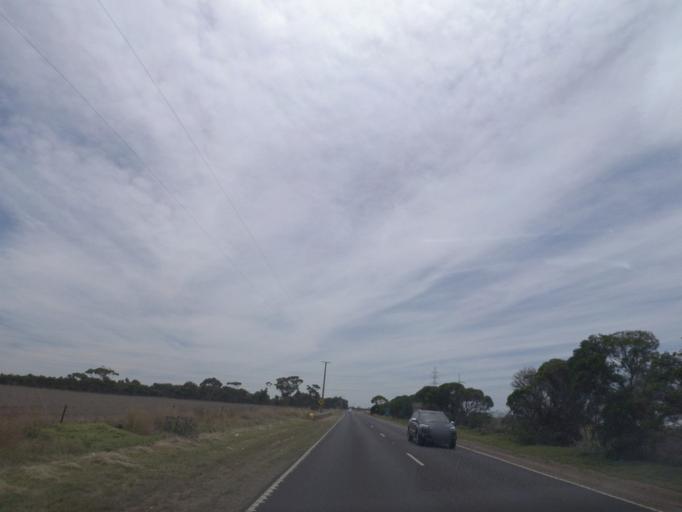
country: AU
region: Victoria
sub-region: Wyndham
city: Truganina
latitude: -37.8076
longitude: 144.6955
